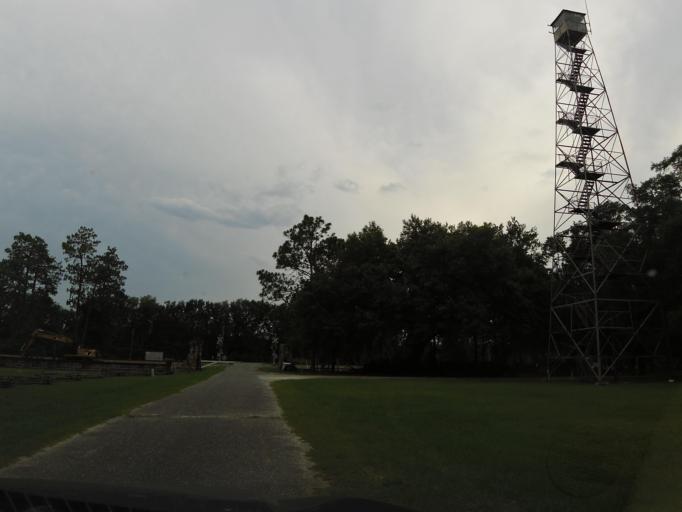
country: US
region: Florida
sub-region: Union County
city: Lake Butler
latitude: 30.2133
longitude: -82.3889
